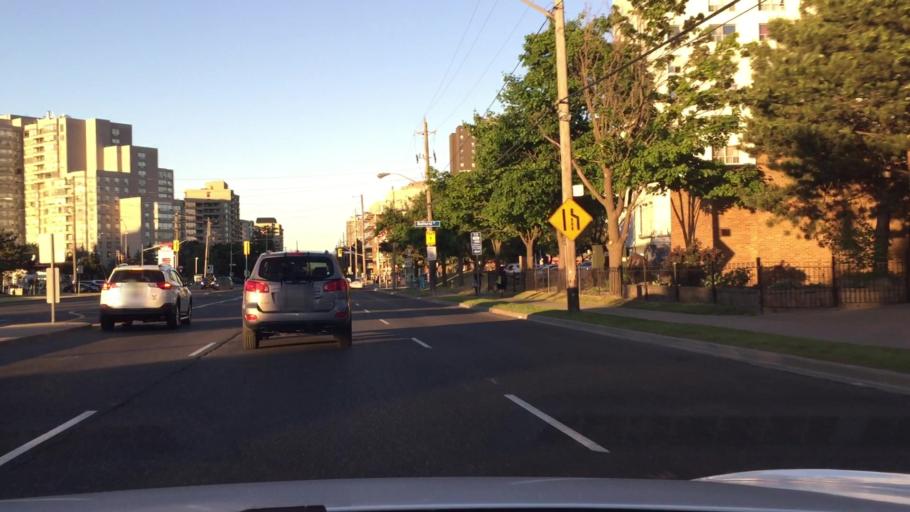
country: CA
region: Ontario
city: Concord
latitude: 43.7920
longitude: -79.4474
